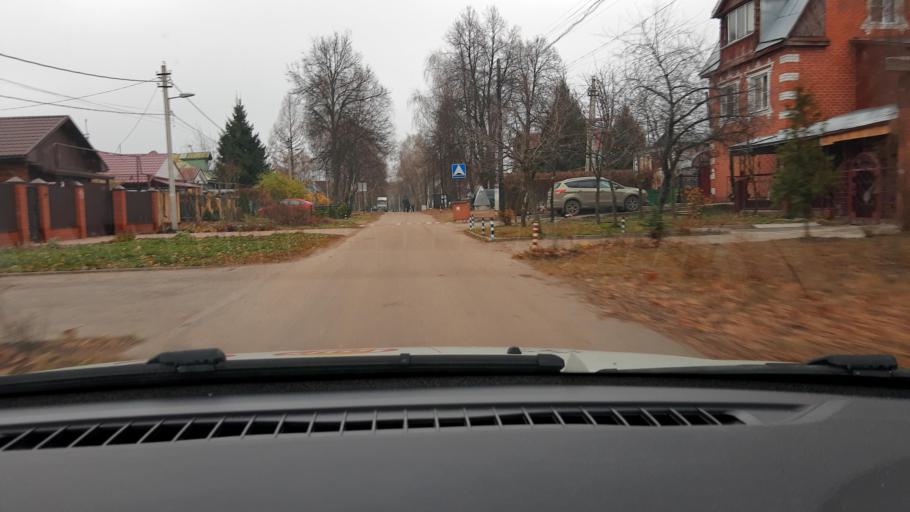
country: RU
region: Nizjnij Novgorod
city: Gorbatovka
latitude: 56.2049
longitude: 43.7662
